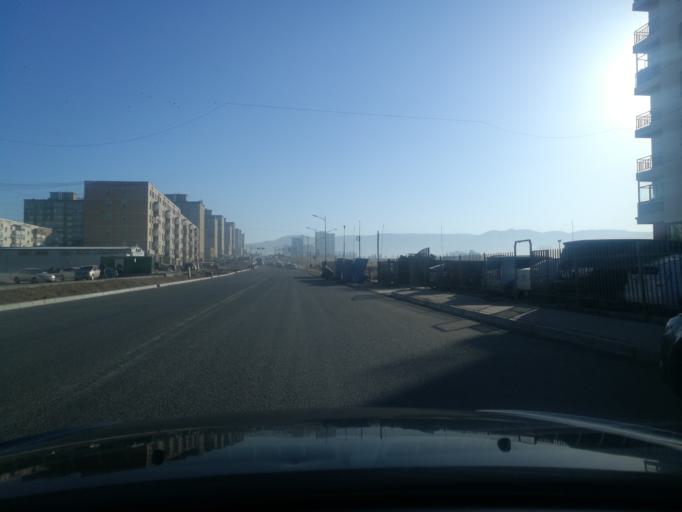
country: MN
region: Ulaanbaatar
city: Ulaanbaatar
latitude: 47.8560
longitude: 106.7591
